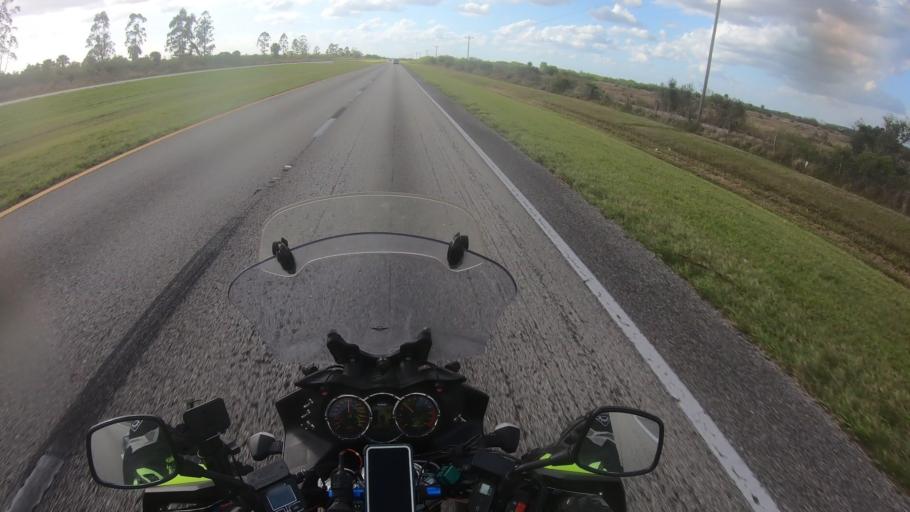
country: US
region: Florida
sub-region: Glades County
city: Moore Haven
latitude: 26.9058
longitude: -81.2589
